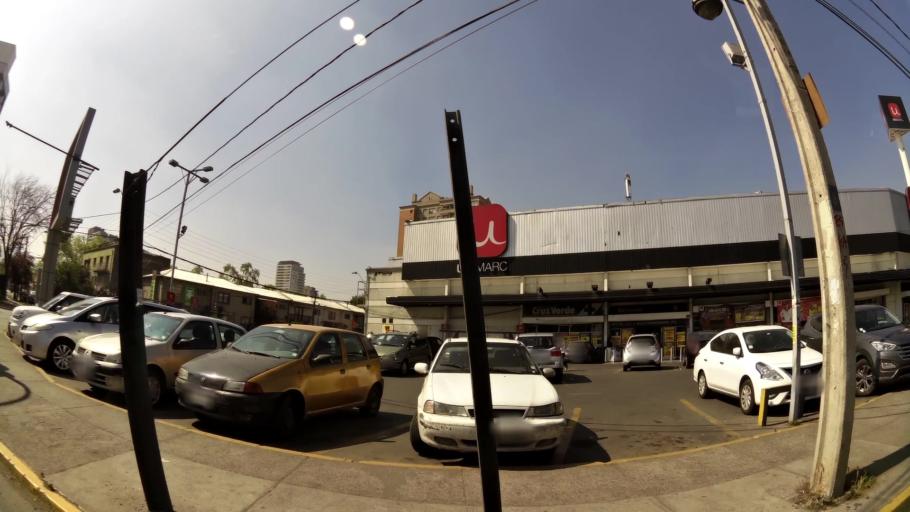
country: CL
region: Santiago Metropolitan
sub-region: Provincia de Santiago
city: Santiago
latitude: -33.4554
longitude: -70.6264
